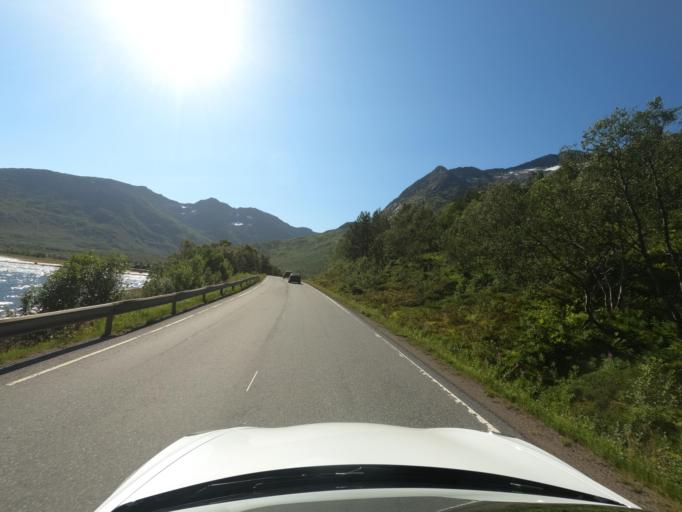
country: NO
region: Nordland
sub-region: Lodingen
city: Lodingen
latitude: 68.5363
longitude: 15.7223
